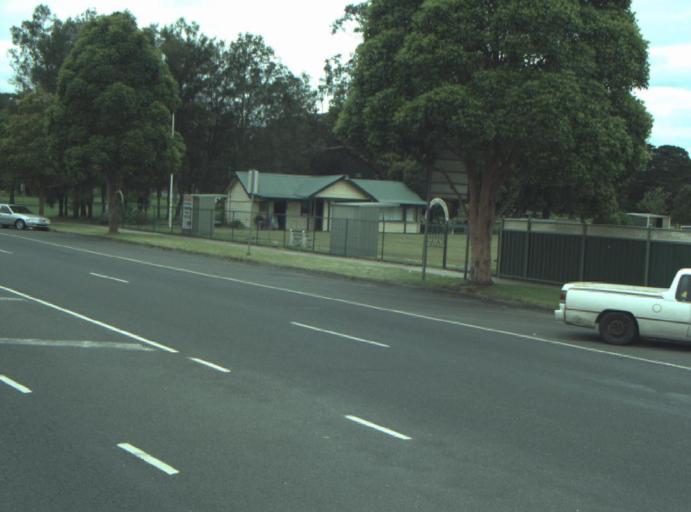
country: AU
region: Victoria
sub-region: Greater Geelong
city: East Geelong
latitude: -38.1518
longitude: 144.3727
